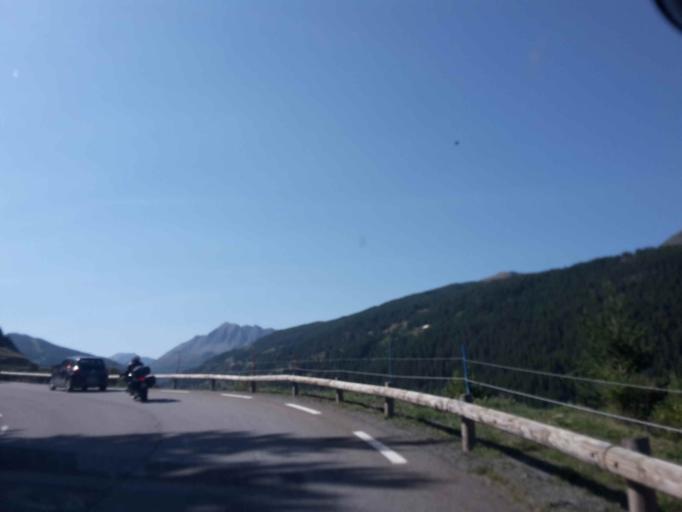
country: FR
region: Provence-Alpes-Cote d'Azur
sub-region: Departement des Hautes-Alpes
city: Guillestre
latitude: 44.6220
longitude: 6.6830
